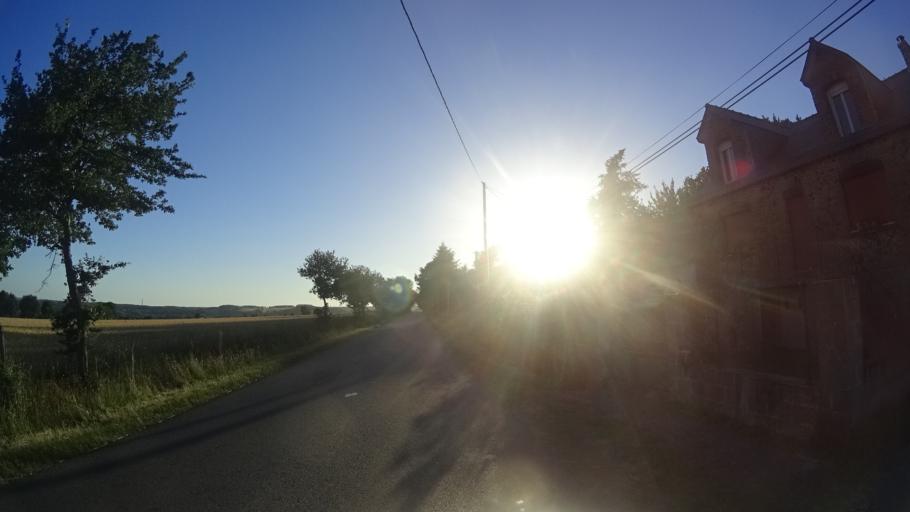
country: FR
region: Brittany
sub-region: Departement d'Ille-et-Vilaine
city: Langon
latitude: 47.7419
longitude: -1.8179
